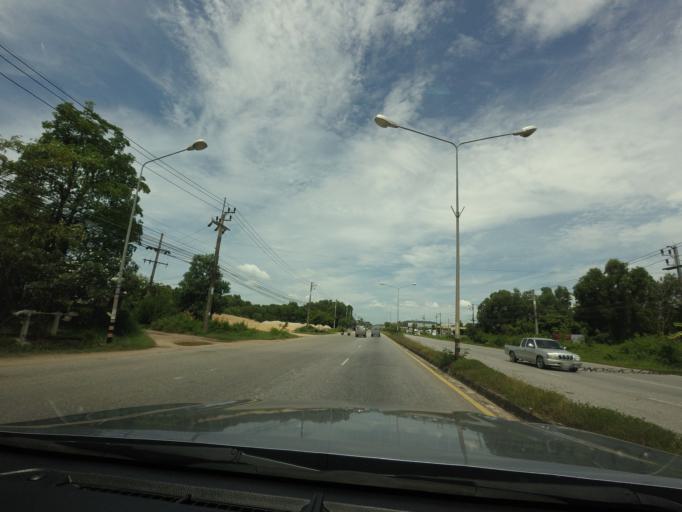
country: TH
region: Songkhla
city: Singhanakhon
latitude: 7.2451
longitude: 100.5414
